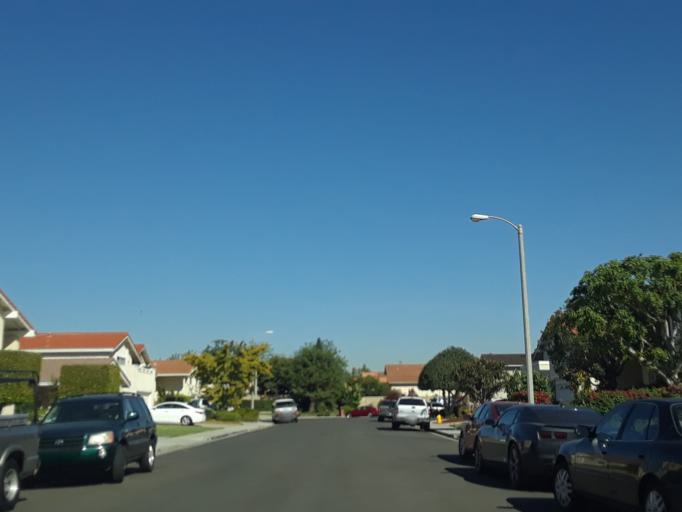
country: US
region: California
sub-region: Orange County
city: Irvine
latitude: 33.7071
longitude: -117.7949
